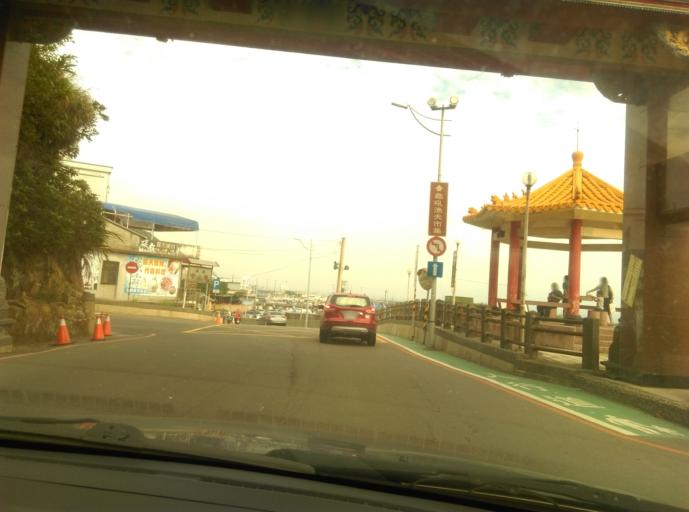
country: TW
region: Taiwan
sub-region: Keelung
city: Keelung
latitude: 25.1940
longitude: 121.6862
